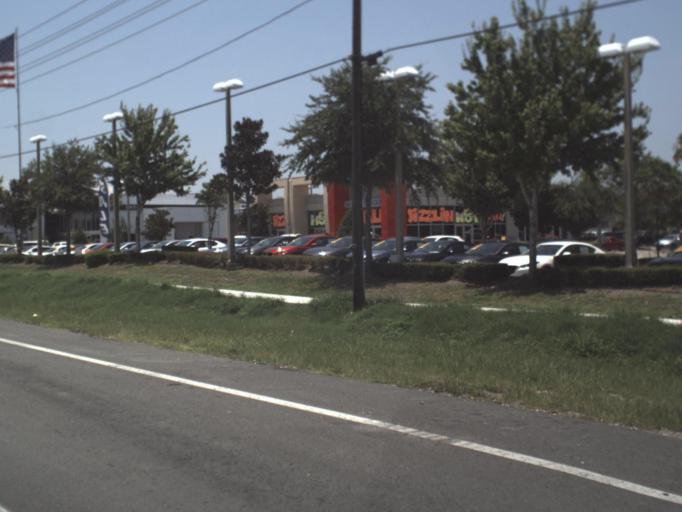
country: US
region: Florida
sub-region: Pasco County
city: Jasmine Estates
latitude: 28.3060
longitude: -82.7020
